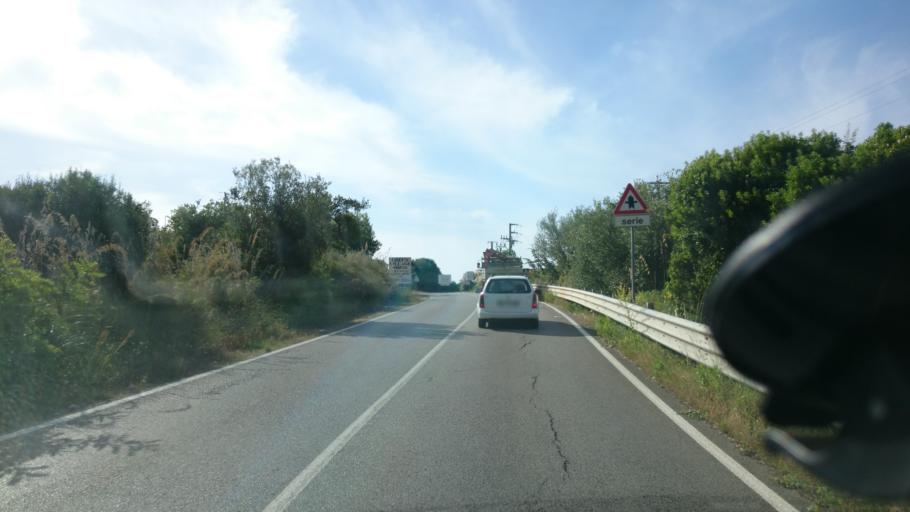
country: IT
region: Campania
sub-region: Provincia di Salerno
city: Marina di Camerota
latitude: 40.0086
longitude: 15.3512
